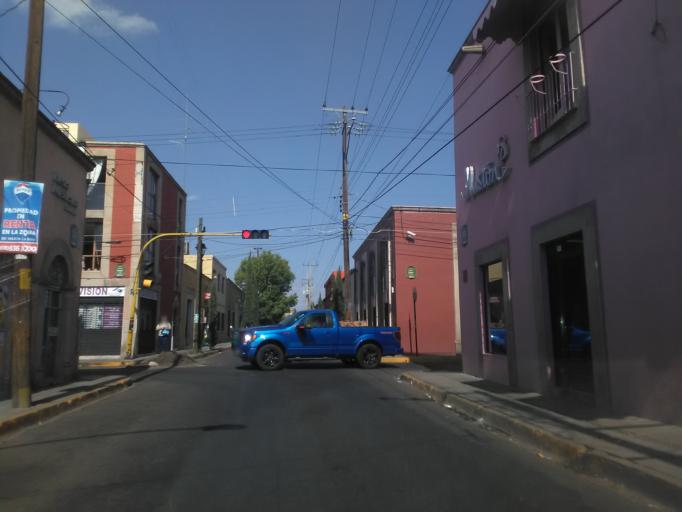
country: MX
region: Durango
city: Victoria de Durango
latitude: 24.0276
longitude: -104.6652
